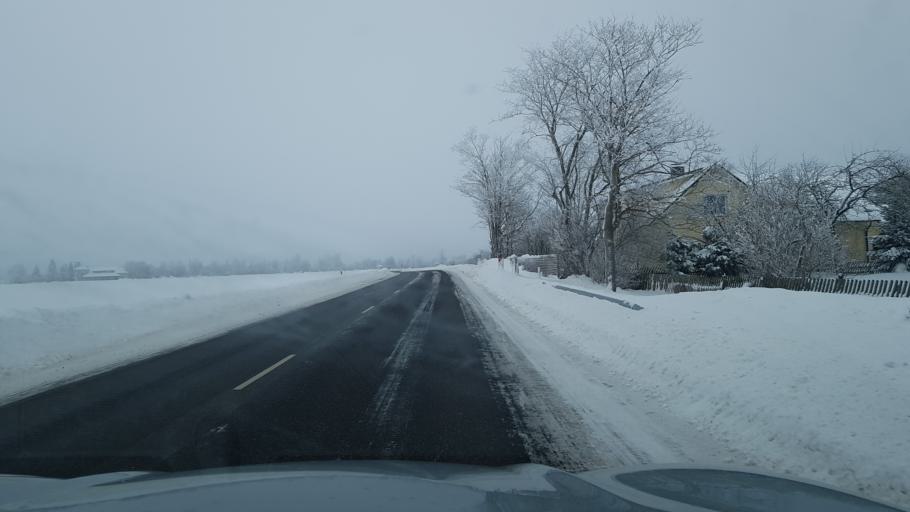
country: EE
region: Ida-Virumaa
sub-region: Johvi vald
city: Johvi
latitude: 59.3246
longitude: 27.3994
